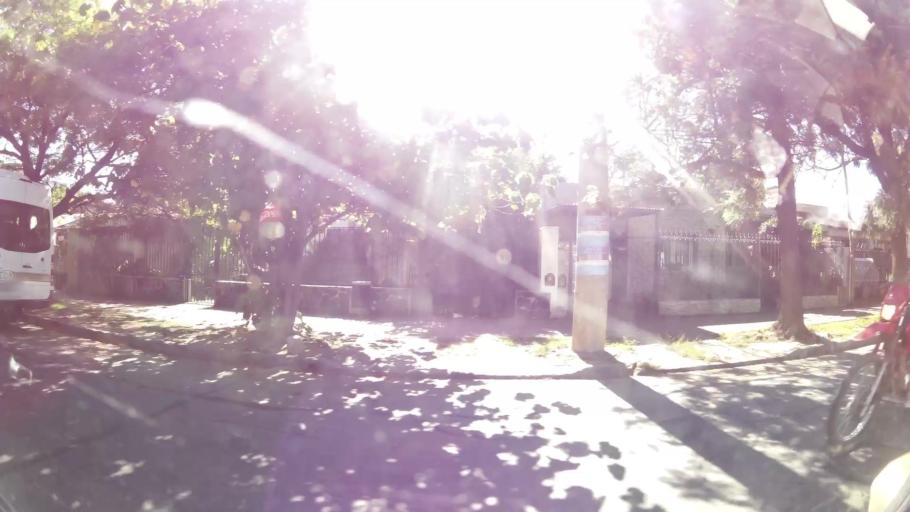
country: AR
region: Cordoba
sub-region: Departamento de Capital
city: Cordoba
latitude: -31.4394
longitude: -64.1688
